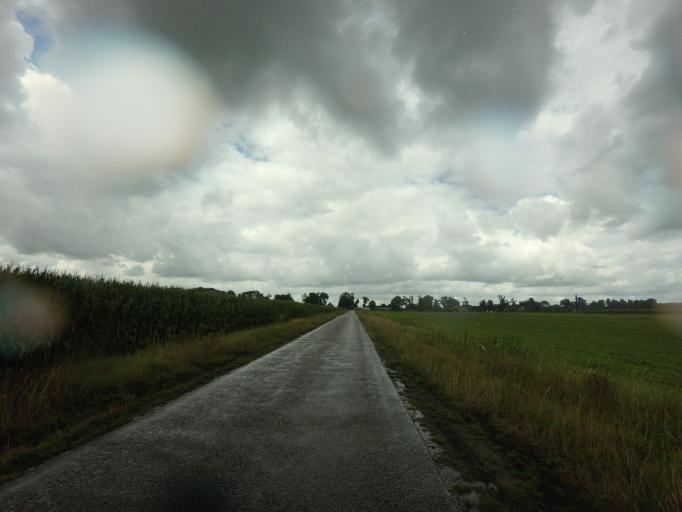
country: NL
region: Overijssel
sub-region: Gemeente Steenwijkerland
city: Wanneperveen
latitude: 52.7201
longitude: 6.1566
